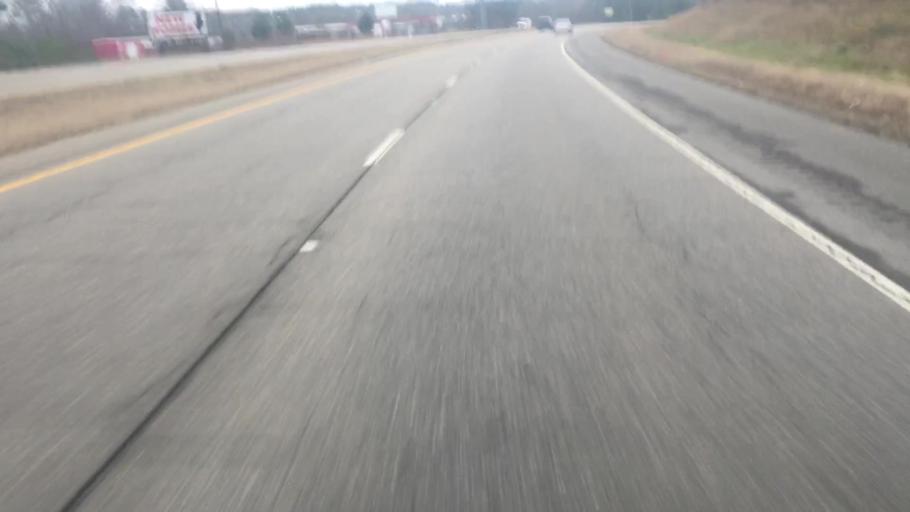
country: US
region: Alabama
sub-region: Walker County
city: Cordova
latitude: 33.8209
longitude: -87.1559
